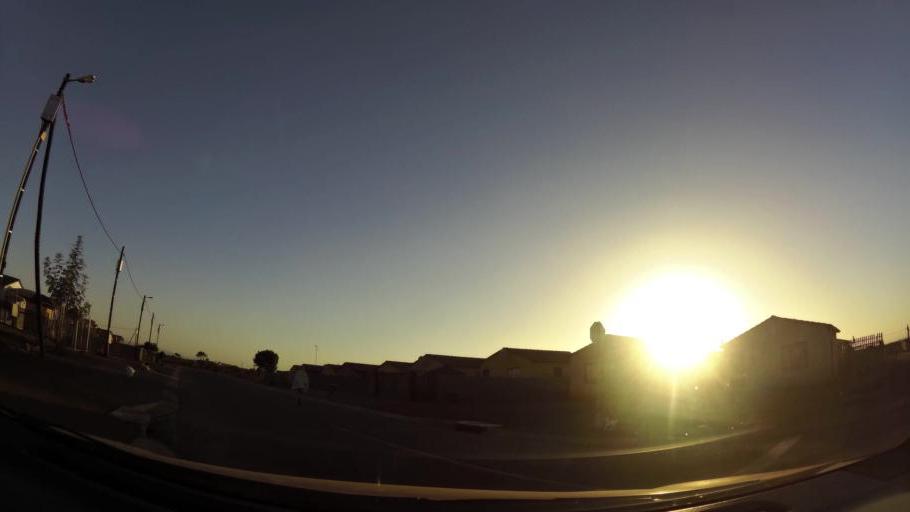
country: ZA
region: Gauteng
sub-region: City of Tshwane Metropolitan Municipality
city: Mabopane
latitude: -25.6019
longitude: 28.0984
